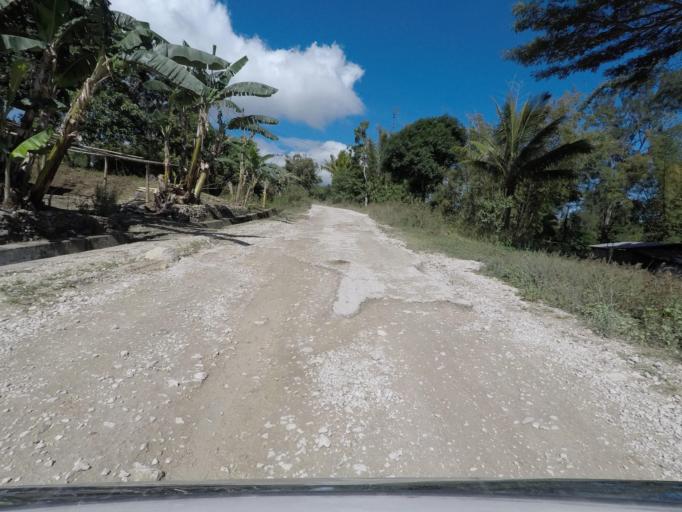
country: TL
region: Baucau
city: Venilale
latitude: -8.6693
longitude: 126.3670
